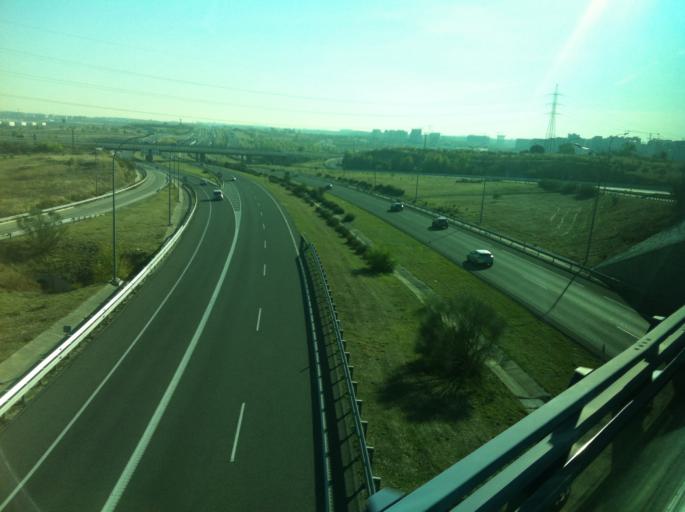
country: ES
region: Madrid
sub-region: Provincia de Madrid
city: San Sebastian de los Reyes
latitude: 40.5097
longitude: -3.6023
